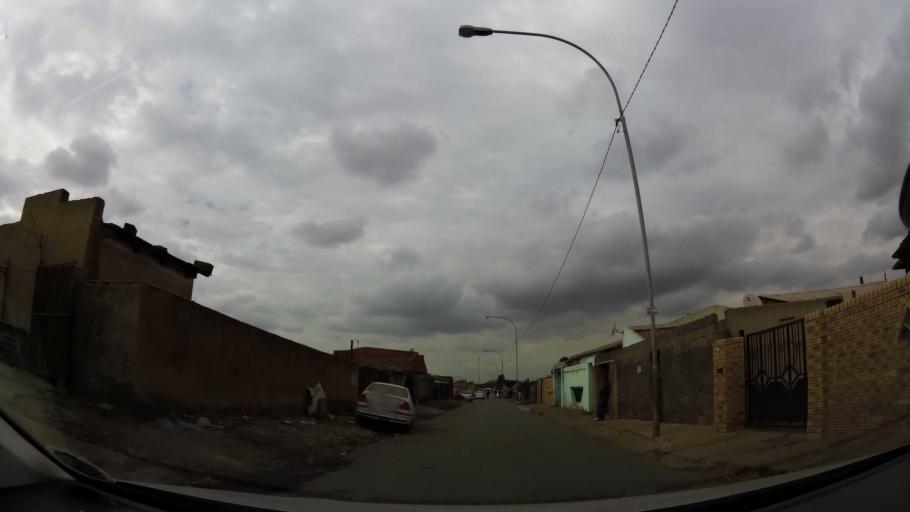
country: ZA
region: Gauteng
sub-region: City of Johannesburg Metropolitan Municipality
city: Soweto
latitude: -26.2781
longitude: 27.8595
